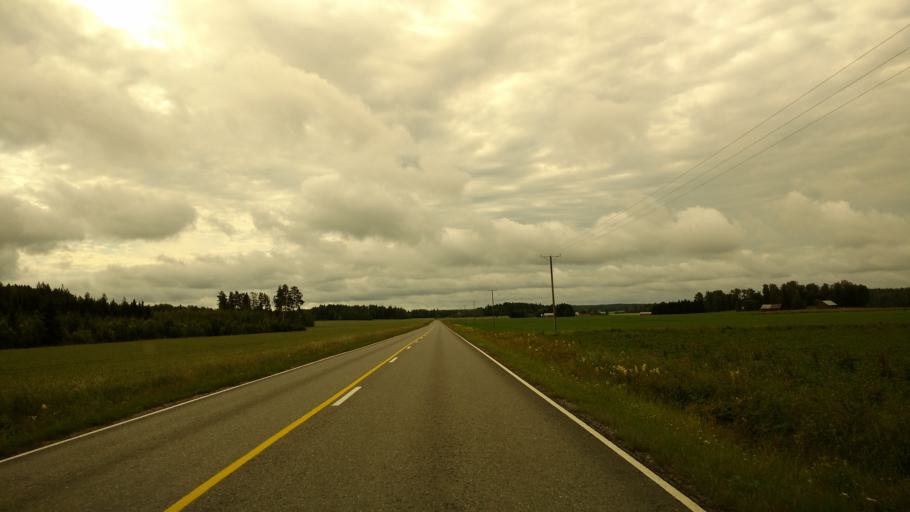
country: FI
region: Varsinais-Suomi
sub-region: Salo
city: Kuusjoki
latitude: 60.4972
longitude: 23.1648
